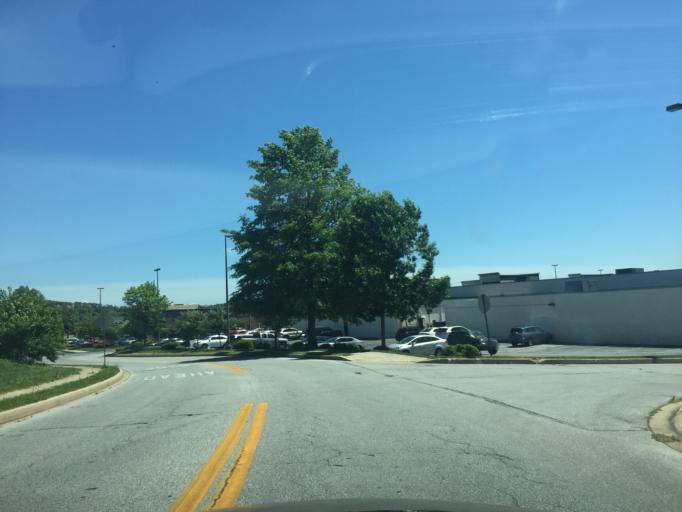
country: US
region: Maryland
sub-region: Carroll County
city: Westminster
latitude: 39.5875
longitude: -76.9890
